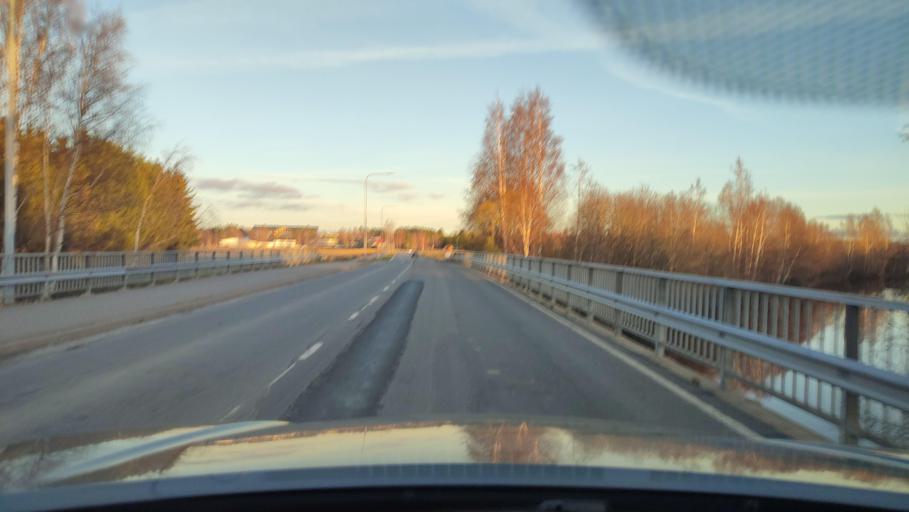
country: FI
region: Ostrobothnia
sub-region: Sydosterbotten
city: Naerpes
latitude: 62.4724
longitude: 21.3408
